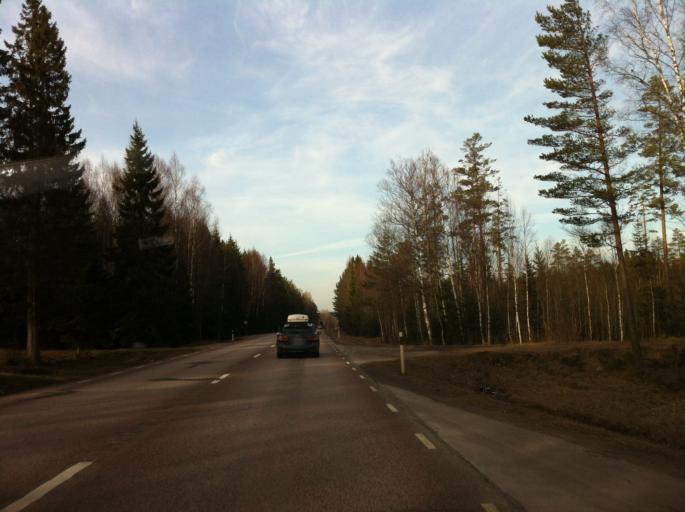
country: SE
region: Vaermland
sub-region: Kristinehamns Kommun
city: Bjorneborg
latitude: 59.2038
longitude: 14.1830
